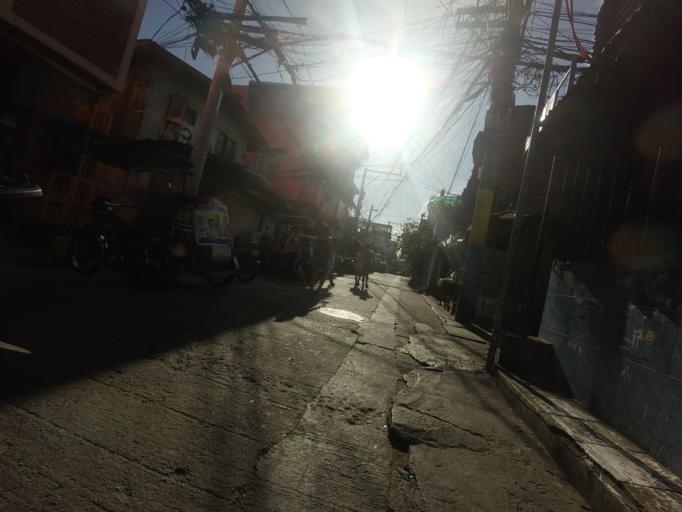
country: PH
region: Metro Manila
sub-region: Mandaluyong
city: Mandaluyong City
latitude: 14.5871
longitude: 121.0286
